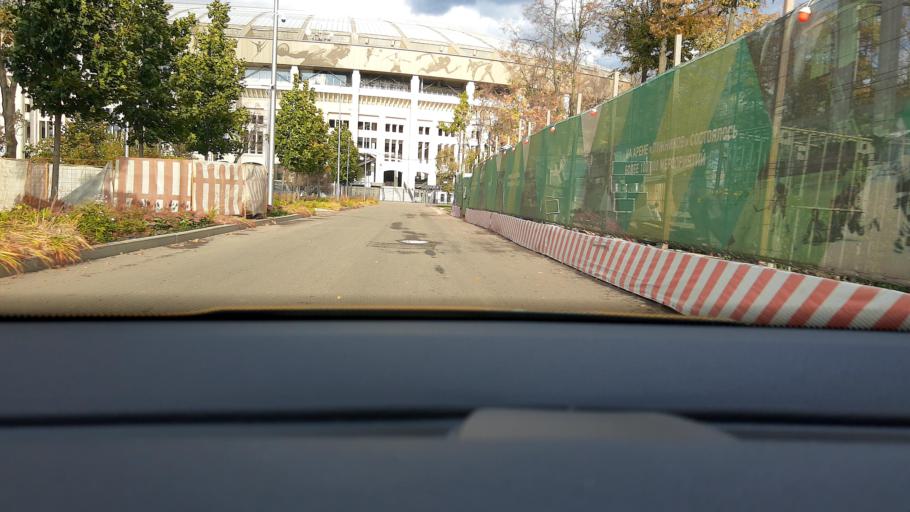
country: RU
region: Moscow
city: Luzhniki
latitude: 55.7136
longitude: 37.5512
